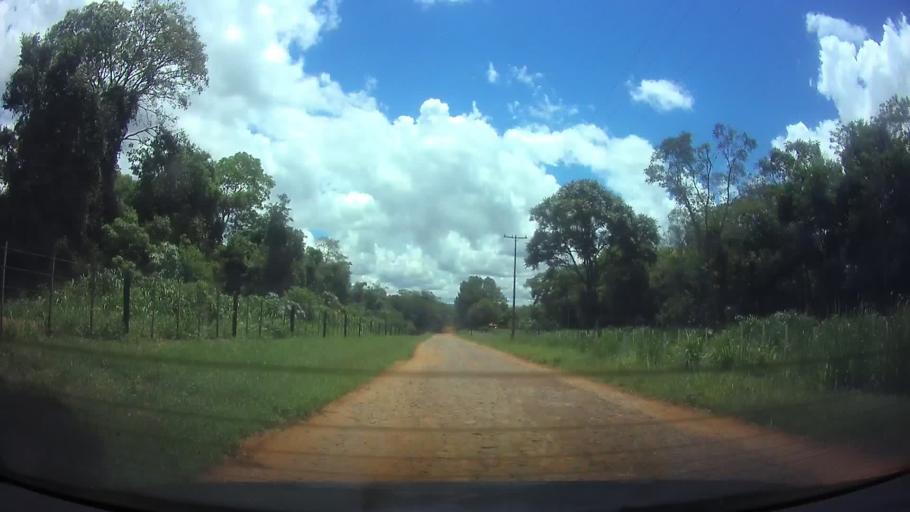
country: PY
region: Paraguari
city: La Colmena
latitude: -25.9193
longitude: -56.7943
